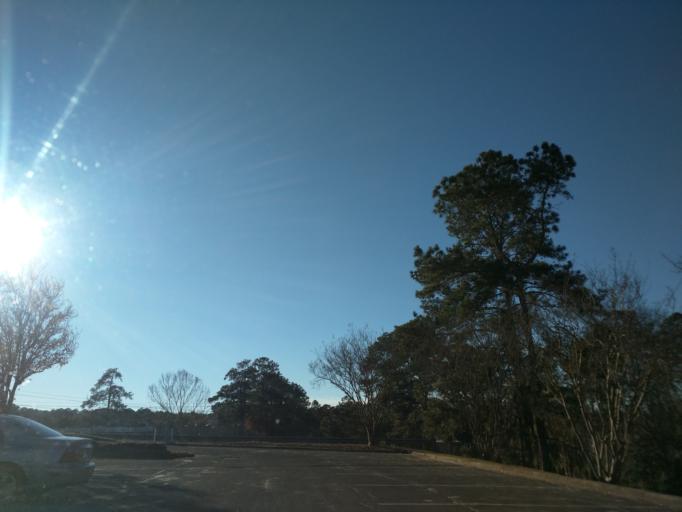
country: US
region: Florida
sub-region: Leon County
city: Tallahassee
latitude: 30.4771
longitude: -84.2931
